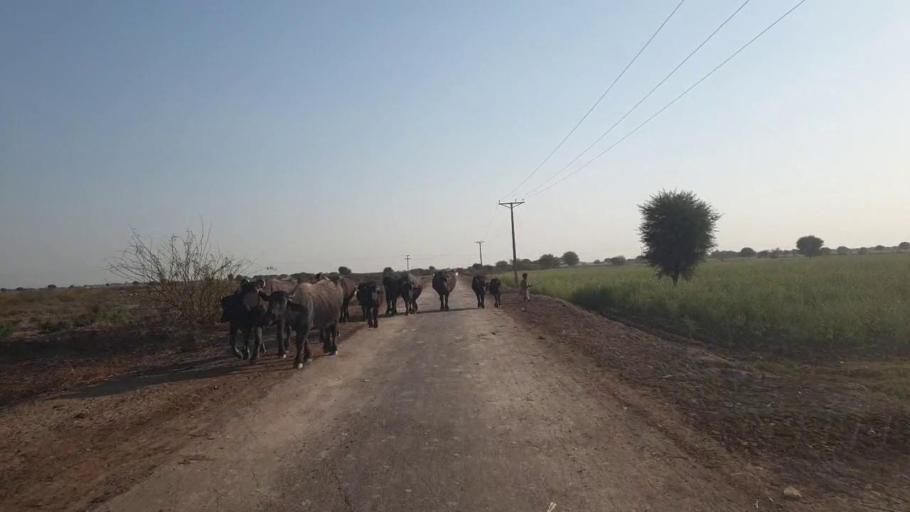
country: PK
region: Sindh
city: Chambar
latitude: 25.2843
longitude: 68.7498
